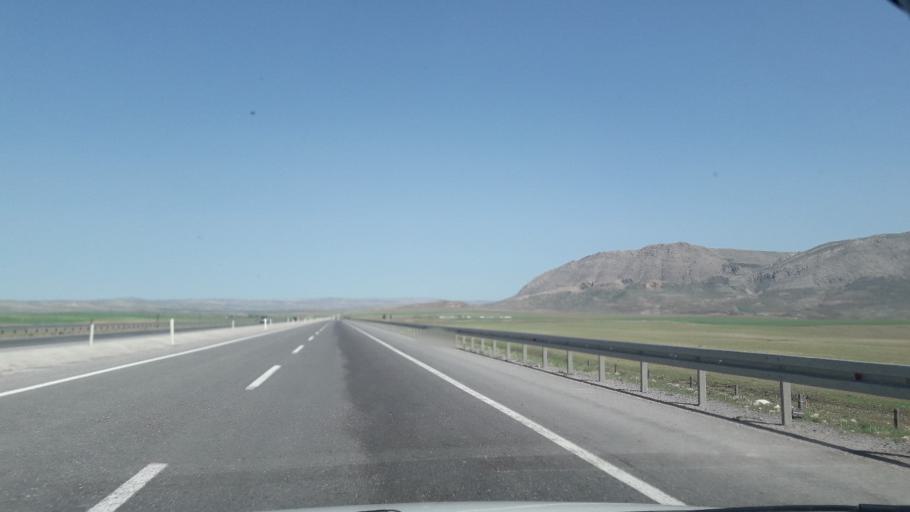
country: TR
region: Sivas
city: Deliktas
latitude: 39.3589
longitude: 37.1297
